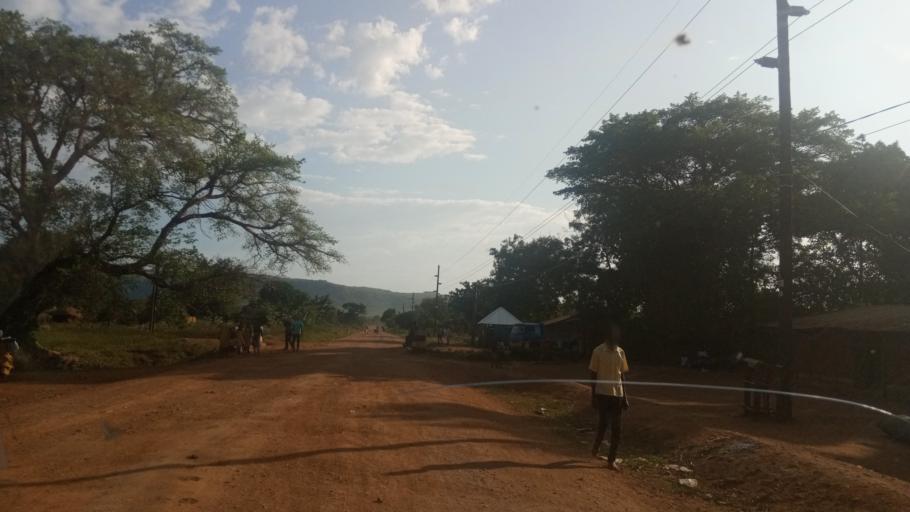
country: UG
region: Eastern Region
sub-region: Kapchorwa District
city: Kapchorwa
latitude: 1.4151
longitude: 34.3498
